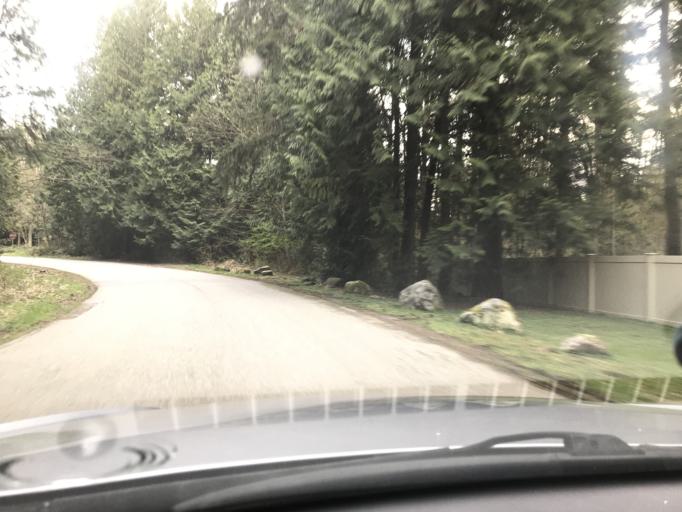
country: US
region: Washington
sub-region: King County
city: Union Hill-Novelty Hill
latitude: 47.6967
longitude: -122.0417
